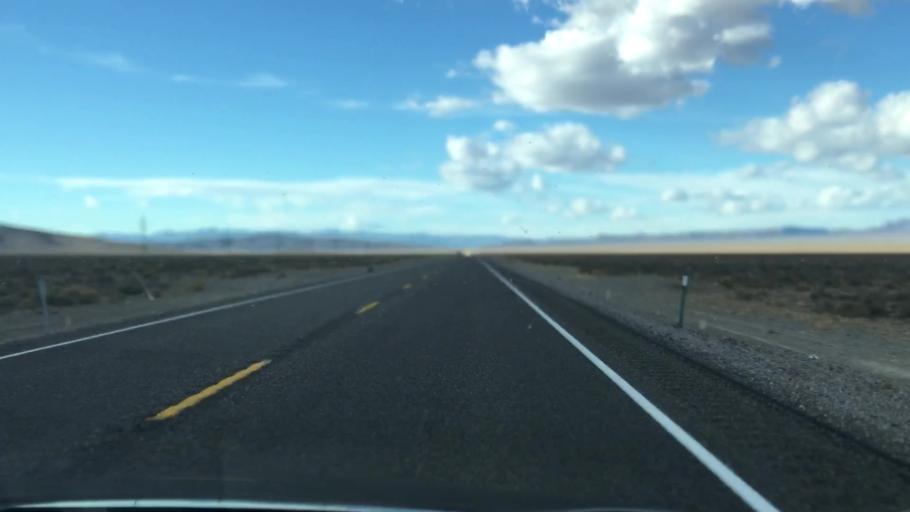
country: US
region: Nevada
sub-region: Nye County
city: Beatty
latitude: 37.1197
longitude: -116.8215
